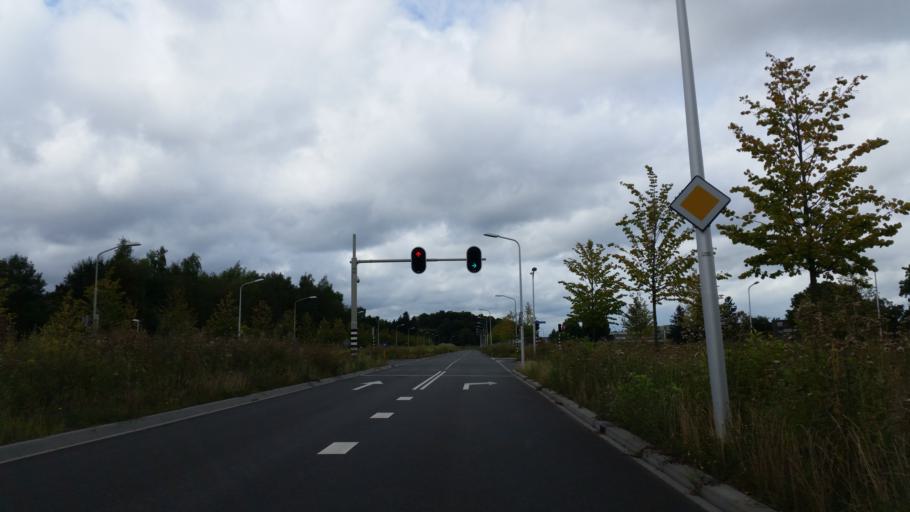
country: NL
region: Limburg
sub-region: Gemeente Maastricht
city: Maastricht
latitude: 50.8606
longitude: 5.6807
